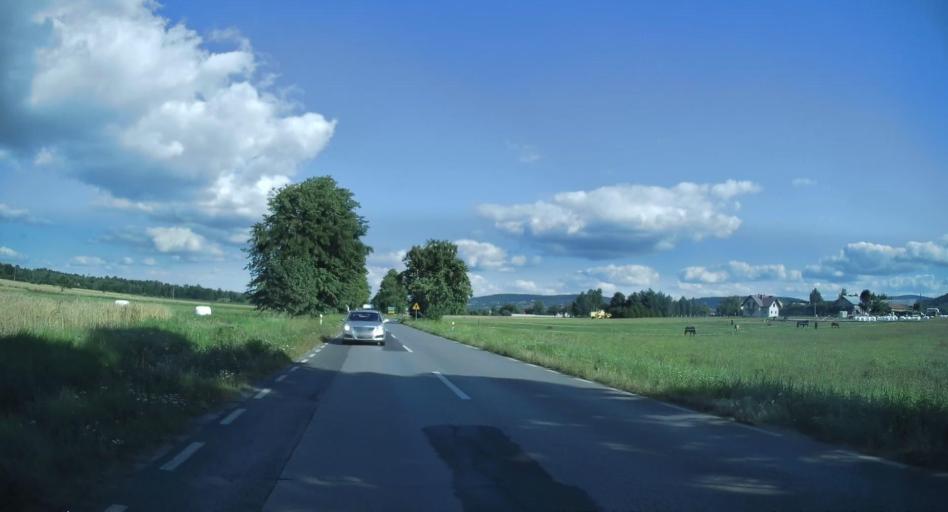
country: PL
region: Swietokrzyskie
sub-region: Powiat kielecki
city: Bodzentyn
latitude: 50.9645
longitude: 20.8956
